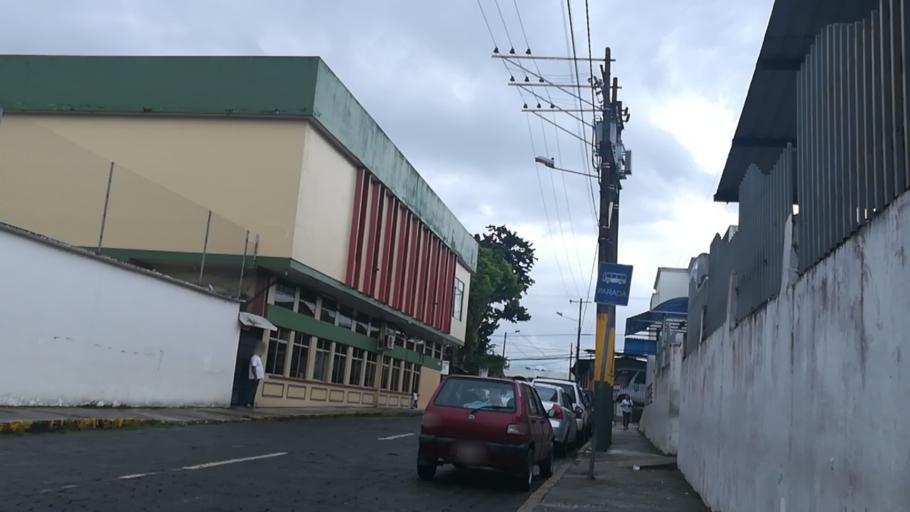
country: EC
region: Napo
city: Tena
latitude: -0.9898
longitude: -77.8160
